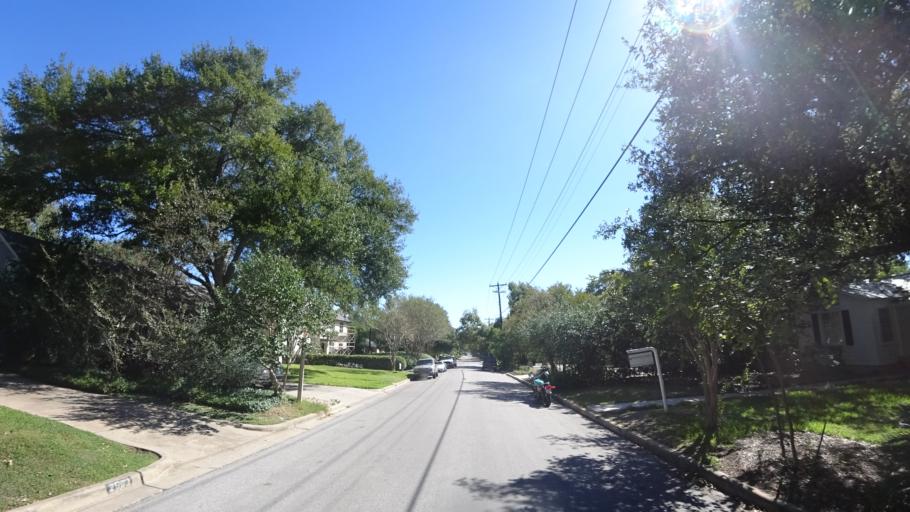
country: US
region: Texas
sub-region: Travis County
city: Rollingwood
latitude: 30.2971
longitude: -97.7657
